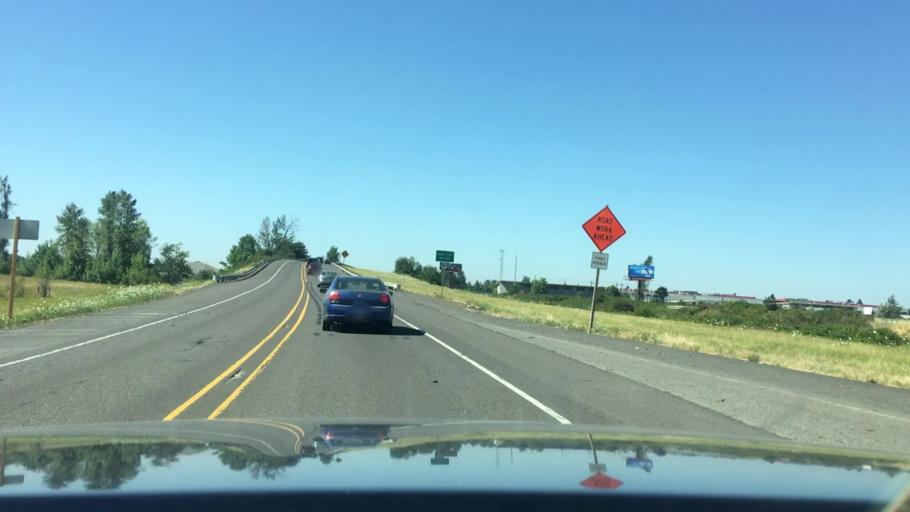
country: US
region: Oregon
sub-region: Lane County
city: Eugene
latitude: 44.0571
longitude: -123.1730
